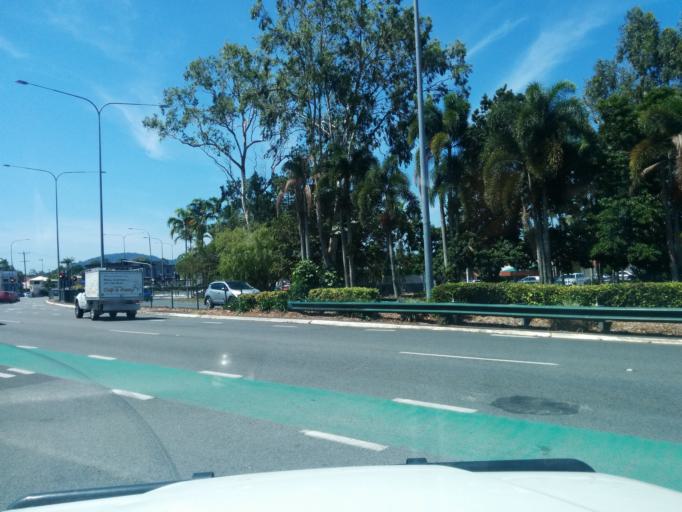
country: AU
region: Queensland
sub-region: Cairns
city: Woree
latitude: -16.9462
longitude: 145.7384
